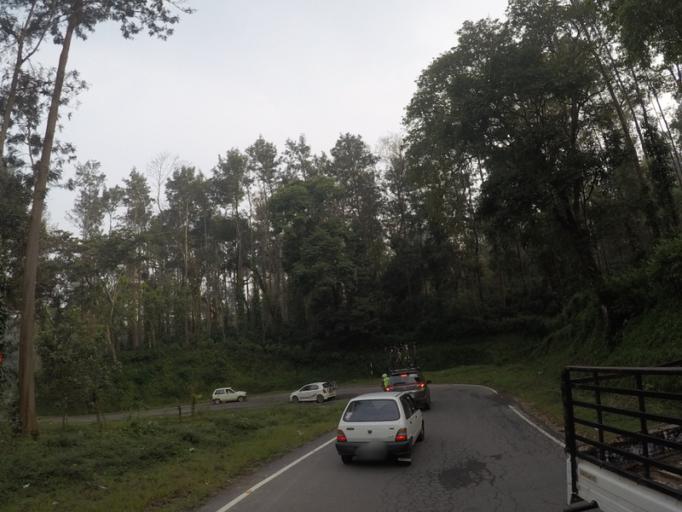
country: IN
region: Karnataka
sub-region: Chikmagalur
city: Mudigere
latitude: 13.2565
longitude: 75.6354
